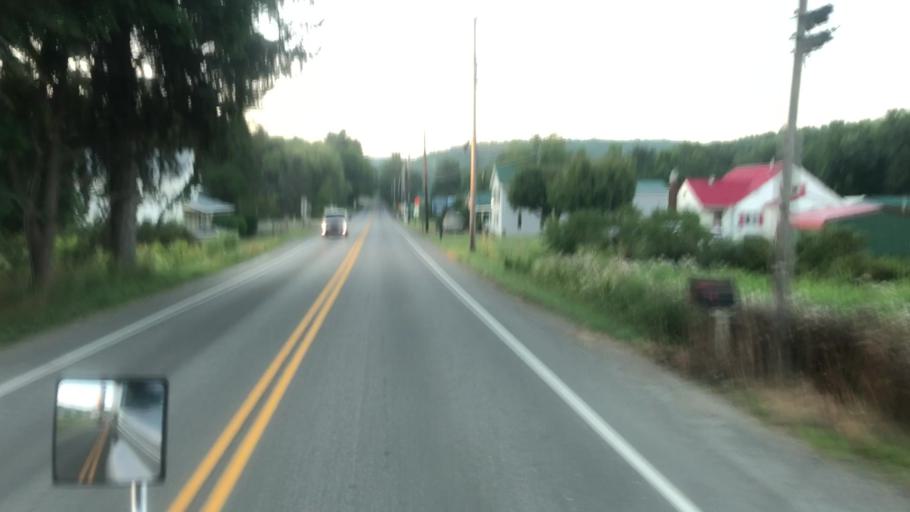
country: US
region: Pennsylvania
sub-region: Crawford County
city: Titusville
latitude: 41.6203
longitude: -79.6407
